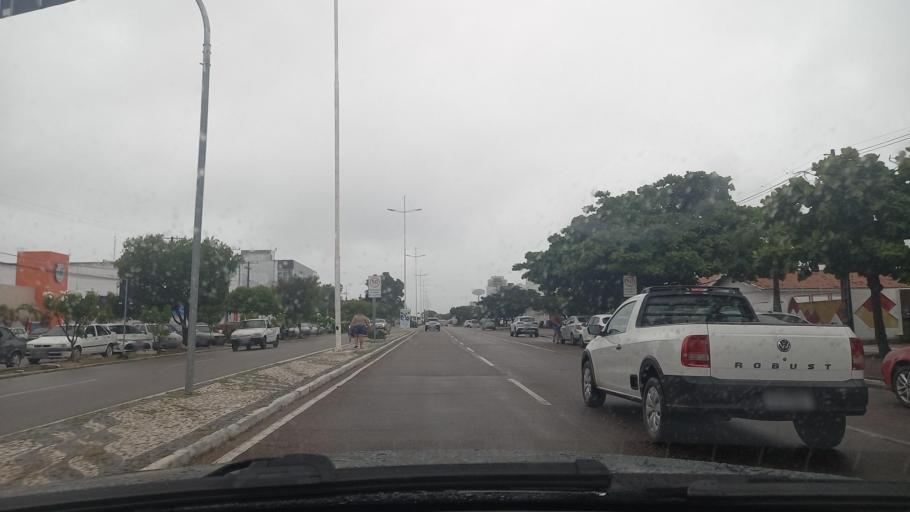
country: BR
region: Bahia
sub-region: Paulo Afonso
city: Paulo Afonso
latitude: -9.3992
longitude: -38.2245
